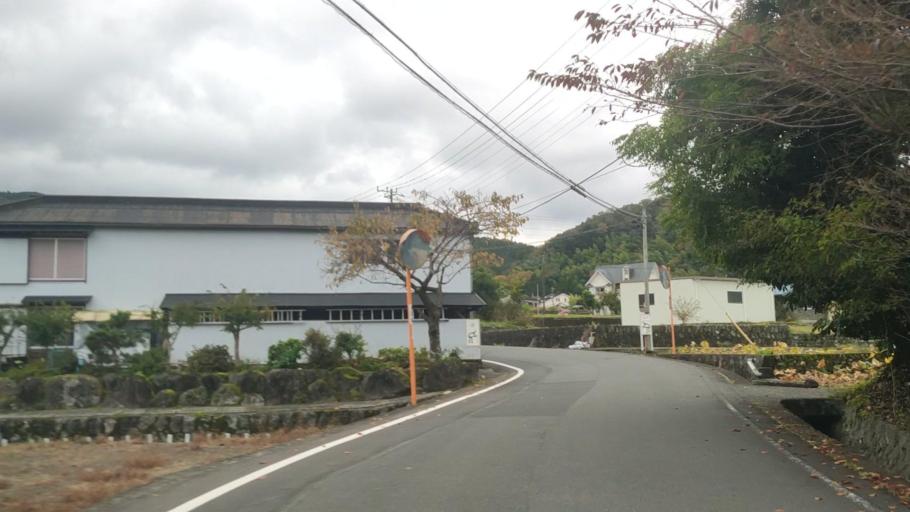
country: JP
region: Shizuoka
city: Ito
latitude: 34.9171
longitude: 138.9927
